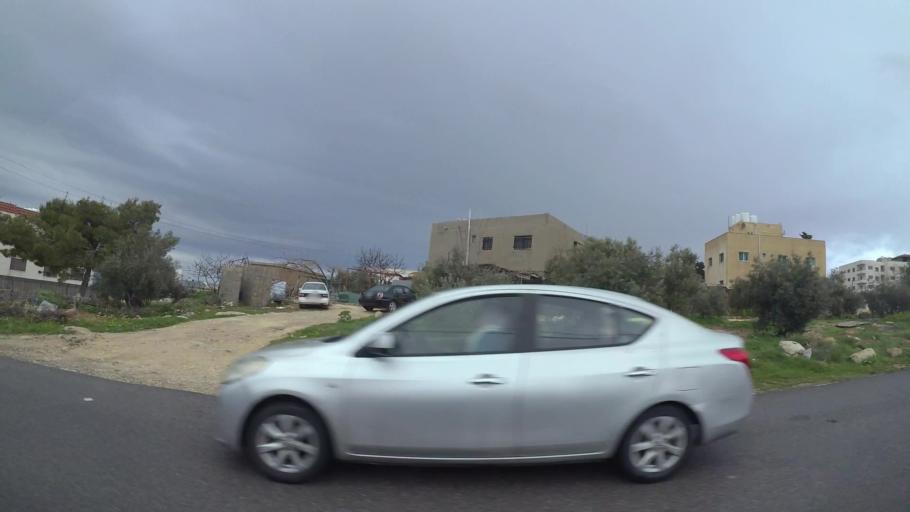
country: JO
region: Amman
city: Al Jubayhah
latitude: 32.0414
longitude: 35.8402
